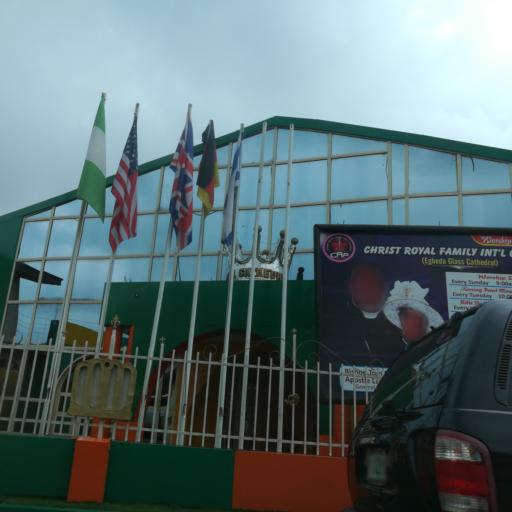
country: NG
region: Lagos
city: Agege
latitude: 6.5910
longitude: 3.2969
